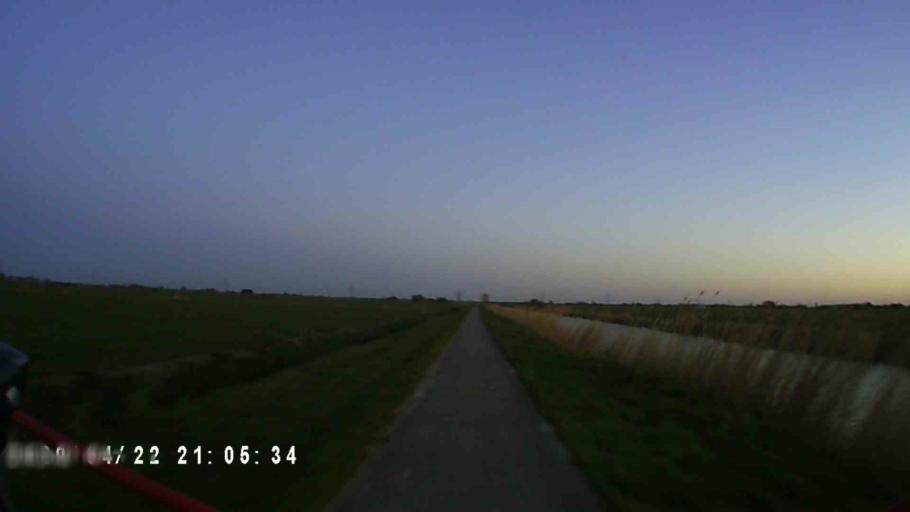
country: NL
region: Groningen
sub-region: Gemeente Winsum
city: Winsum
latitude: 53.3185
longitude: 6.5628
